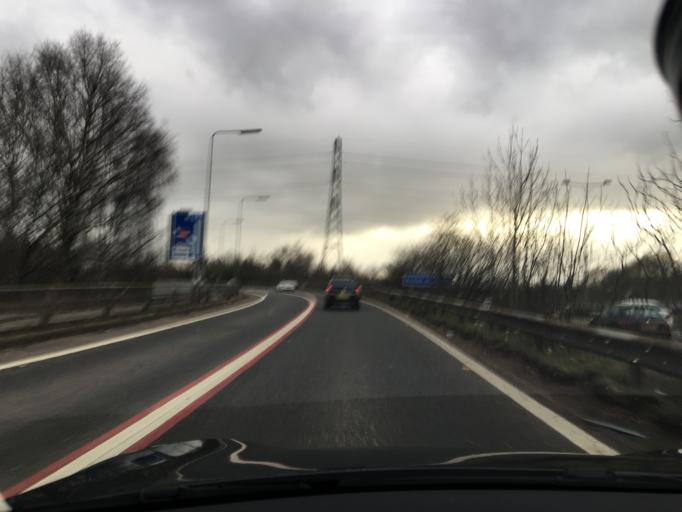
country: GB
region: England
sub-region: Manchester
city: Chorlton cum Hardy
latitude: 53.4167
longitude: -2.2627
